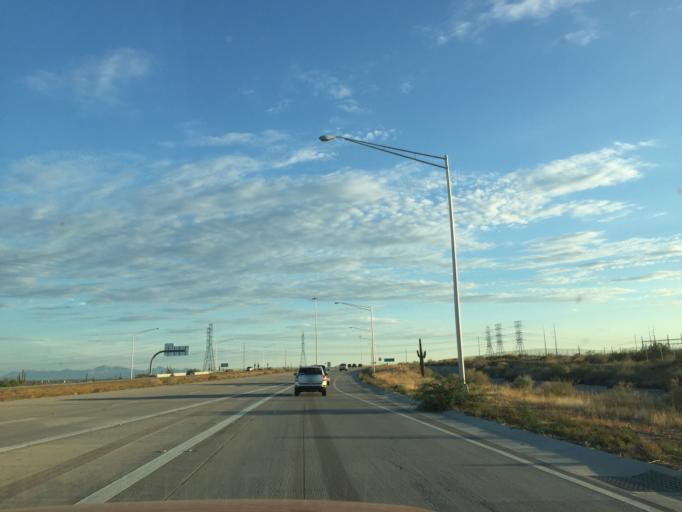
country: US
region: Arizona
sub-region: Maricopa County
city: Sun City West
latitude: 33.7102
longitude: -112.3125
